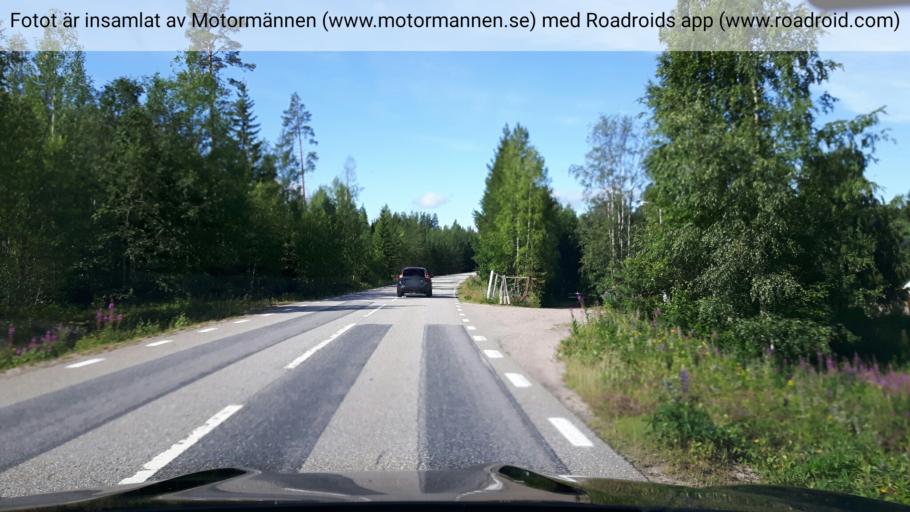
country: SE
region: Gaevleborg
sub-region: Ljusdals Kommun
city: Farila
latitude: 61.7882
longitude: 15.6352
